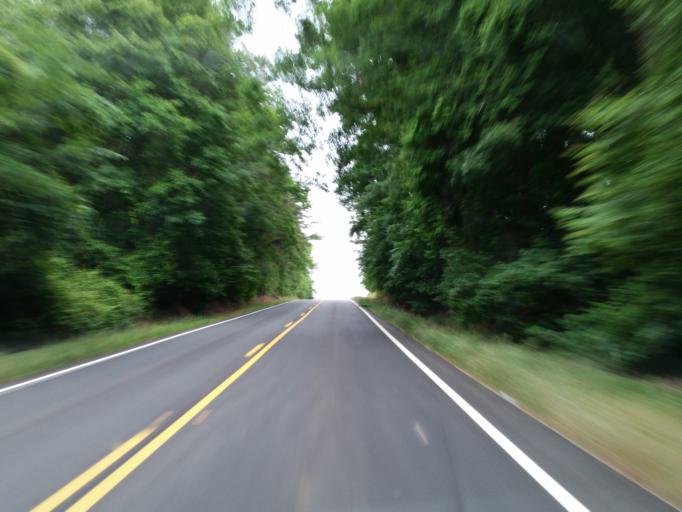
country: US
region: Georgia
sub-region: Dooly County
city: Unadilla
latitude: 32.3177
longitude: -83.7749
